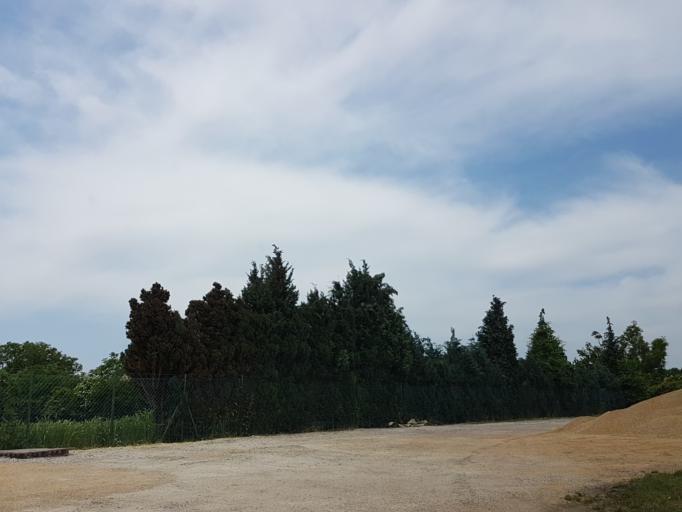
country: HU
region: Veszprem
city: Revfueloep
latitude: 46.8321
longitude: 17.6141
